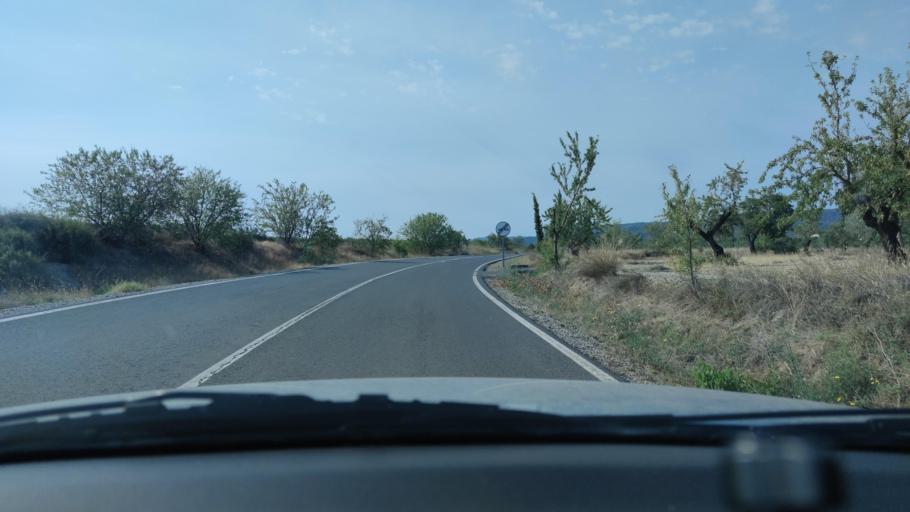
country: ES
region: Catalonia
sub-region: Provincia de Lleida
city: Arbeca
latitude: 41.5001
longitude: 0.8736
